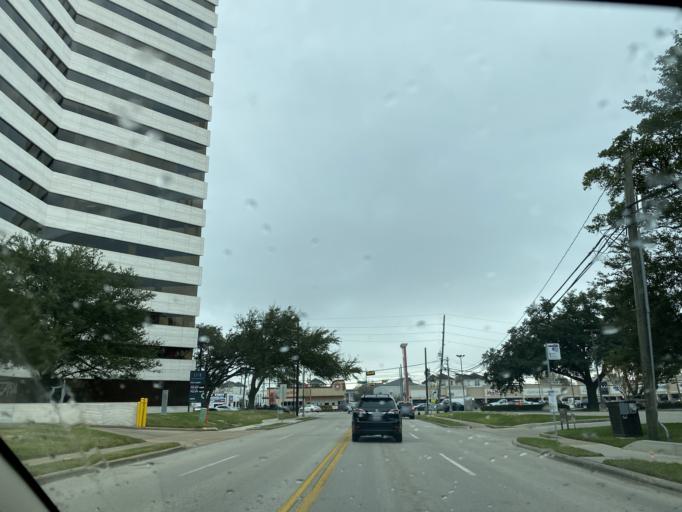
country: US
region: Texas
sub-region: Harris County
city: Hunters Creek Village
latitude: 29.7388
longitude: -95.4794
